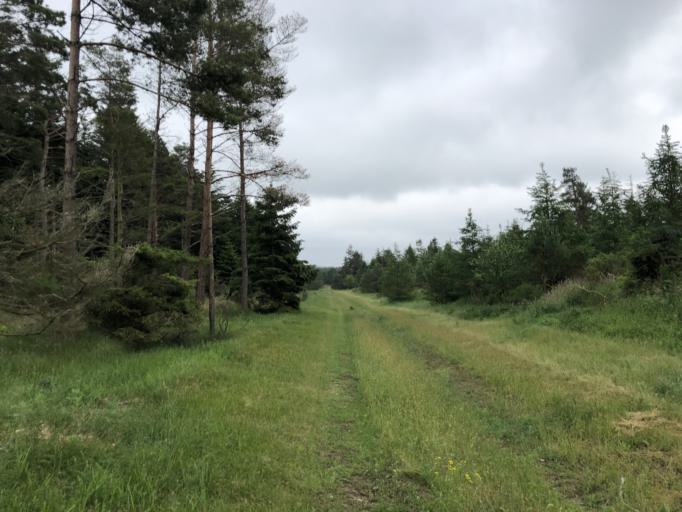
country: DK
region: Central Jutland
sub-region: Holstebro Kommune
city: Ulfborg
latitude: 56.2509
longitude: 8.3604
